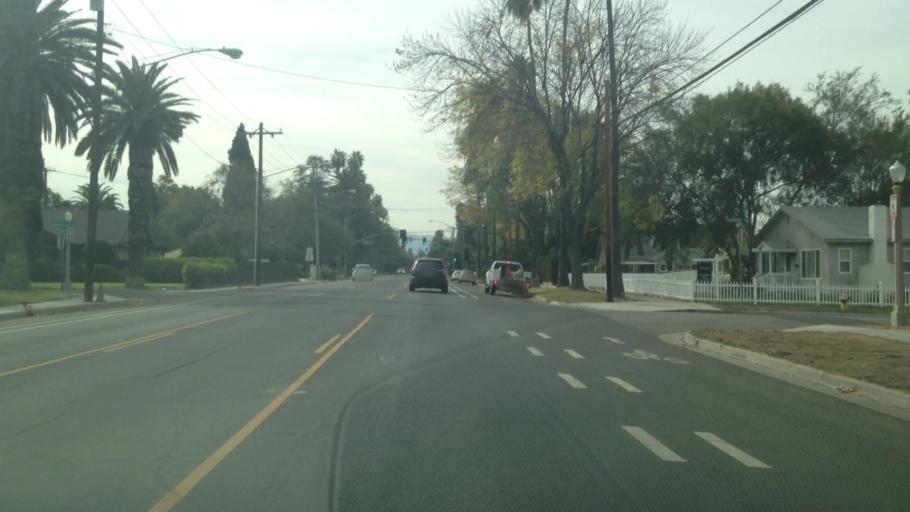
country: US
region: California
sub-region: Riverside County
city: Riverside
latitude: 33.9692
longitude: -117.3913
